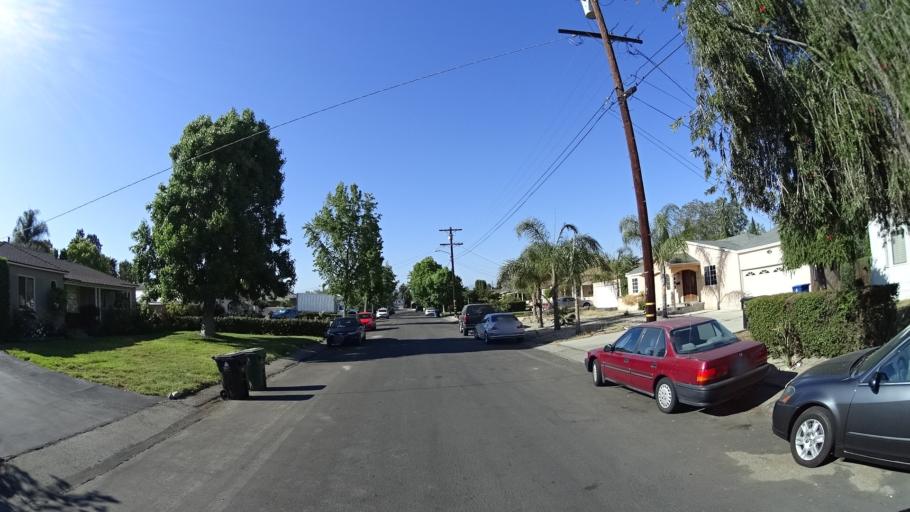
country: US
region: California
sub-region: Los Angeles County
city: North Hollywood
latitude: 34.1799
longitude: -118.3758
